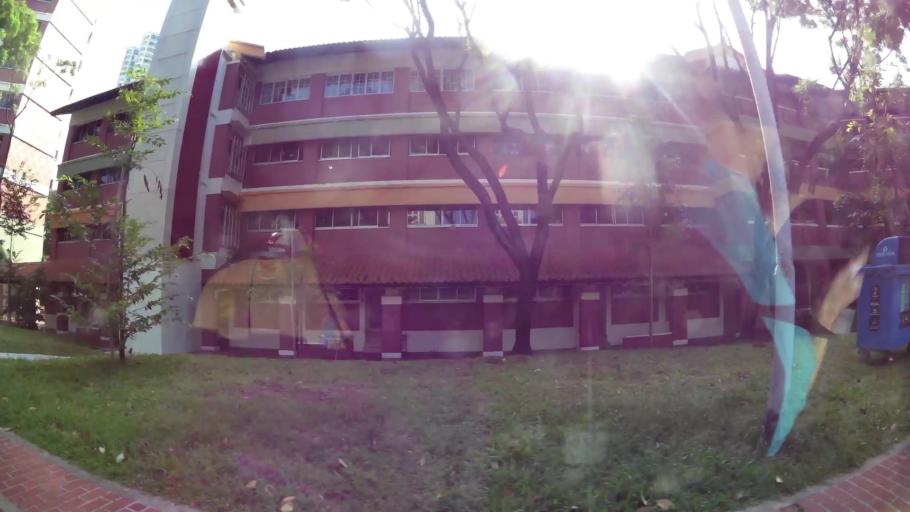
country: SG
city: Singapore
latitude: 1.3580
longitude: 103.8438
